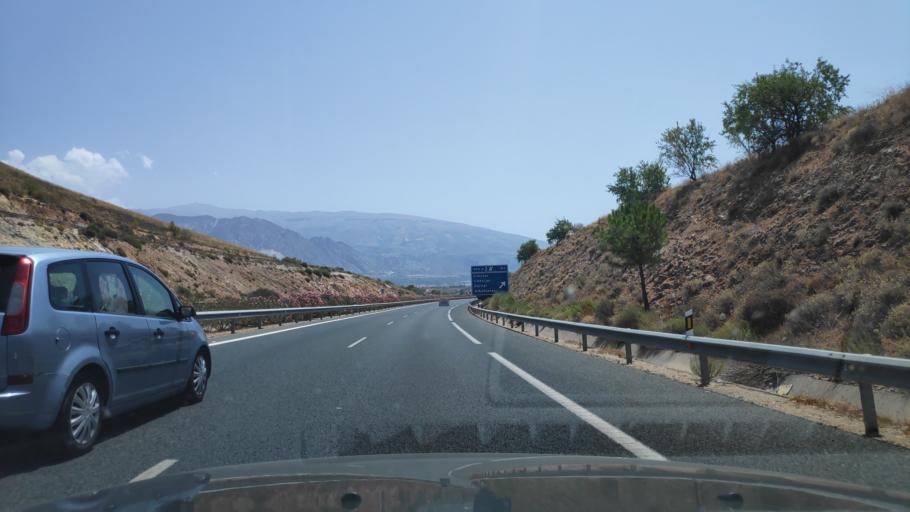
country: ES
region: Andalusia
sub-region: Provincia de Granada
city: Padul
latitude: 36.9910
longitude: -3.6168
